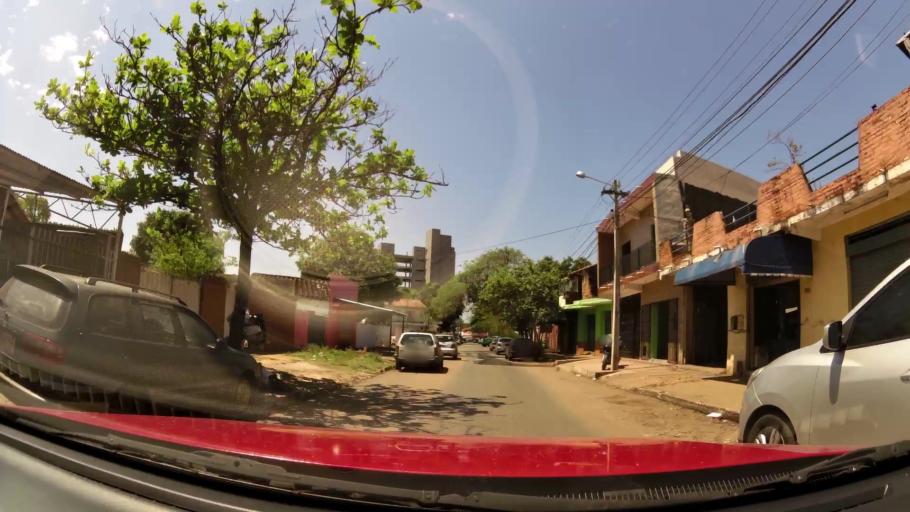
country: PY
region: Central
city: Fernando de la Mora
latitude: -25.3234
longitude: -57.5578
